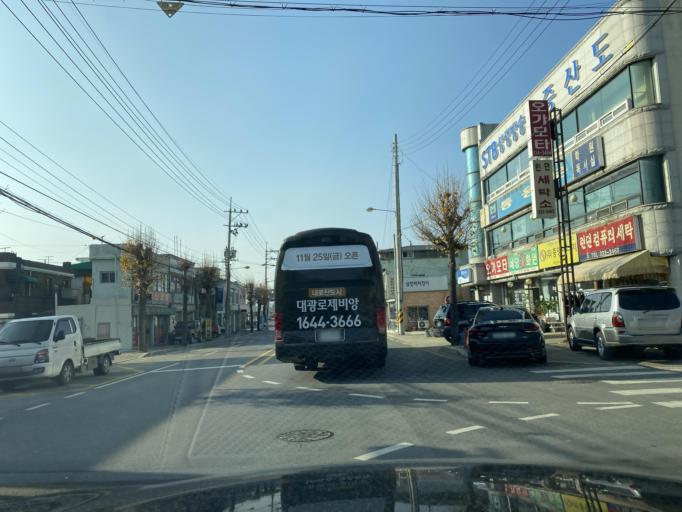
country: KR
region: Chungcheongnam-do
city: Yesan
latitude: 36.6822
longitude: 126.8303
